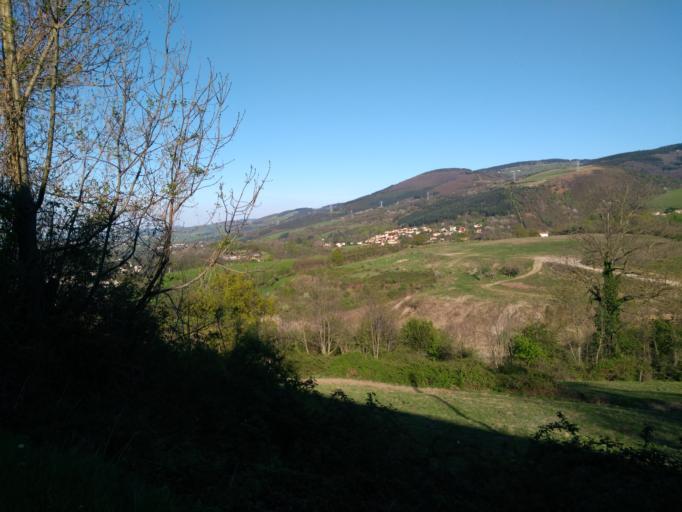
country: FR
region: Rhone-Alpes
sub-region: Departement de la Loire
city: Saint-Etienne
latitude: 45.4269
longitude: 4.4219
